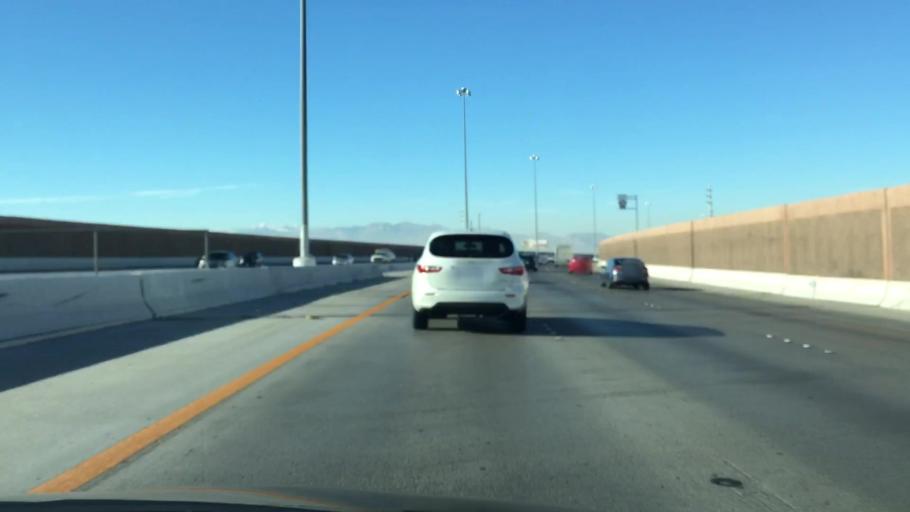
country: US
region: Nevada
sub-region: Clark County
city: Whitney
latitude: 36.0259
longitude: -115.1276
